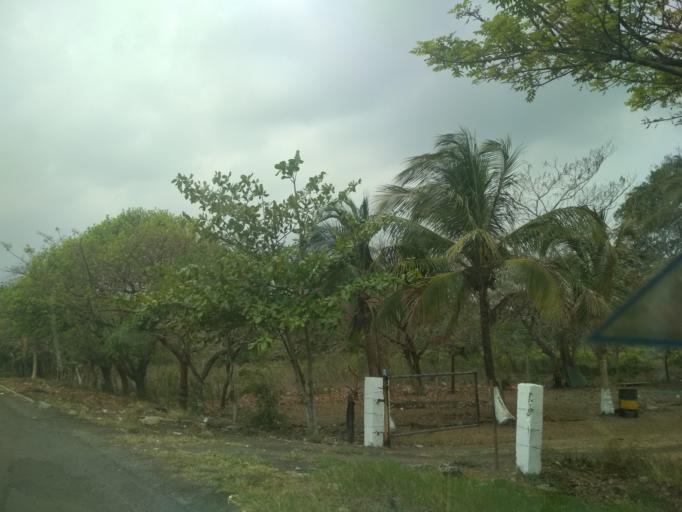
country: MX
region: Veracruz
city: Paso del Toro
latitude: 19.0184
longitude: -96.1373
